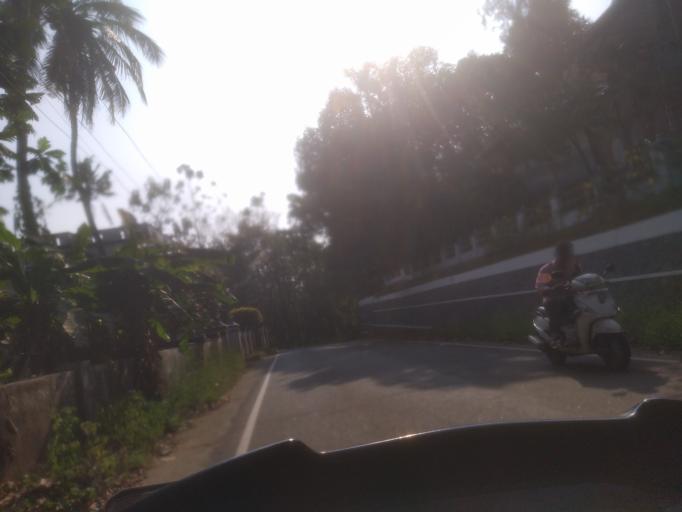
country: IN
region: Kerala
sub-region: Ernakulam
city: Piravam
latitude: 9.8654
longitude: 76.5358
